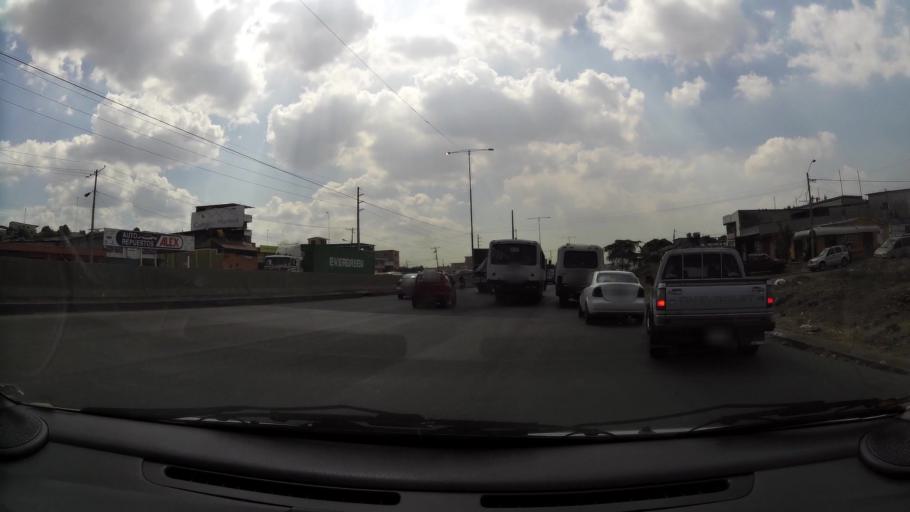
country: EC
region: Guayas
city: Santa Lucia
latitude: -2.1287
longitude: -79.9491
